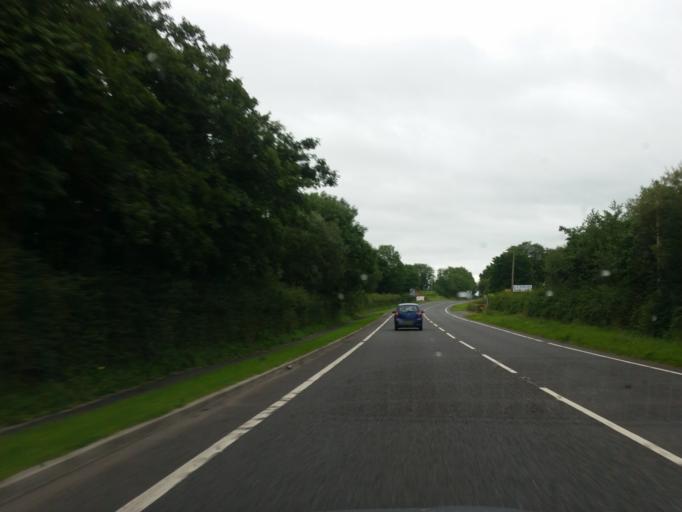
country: GB
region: Northern Ireland
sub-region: Fermanagh District
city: Enniskillen
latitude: 54.3179
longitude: -7.5704
